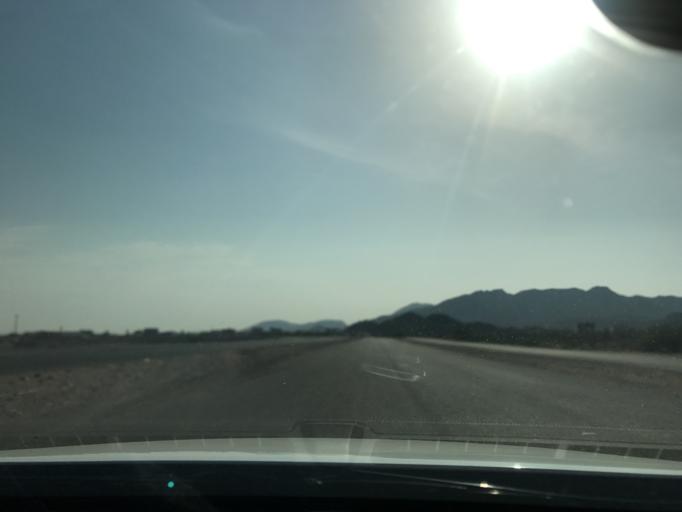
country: SA
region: Makkah
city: Al Jumum
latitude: 21.4520
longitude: 39.5271
